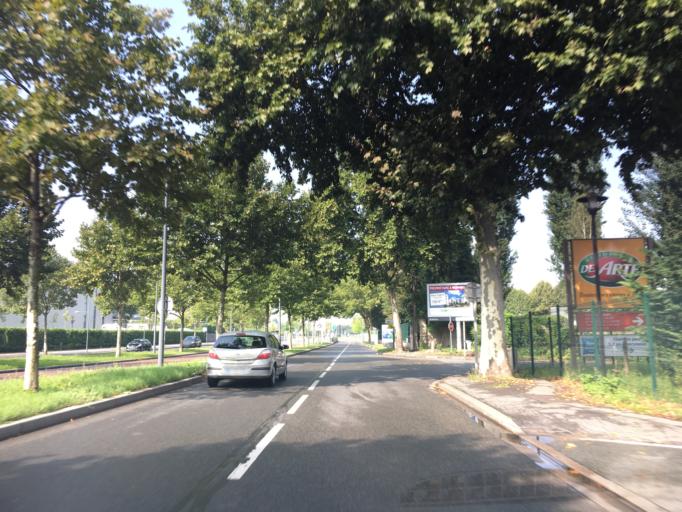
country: FR
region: Ile-de-France
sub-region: Departement du Val-de-Marne
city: Bonneuil-sur-Marne
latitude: 48.7731
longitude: 2.4981
